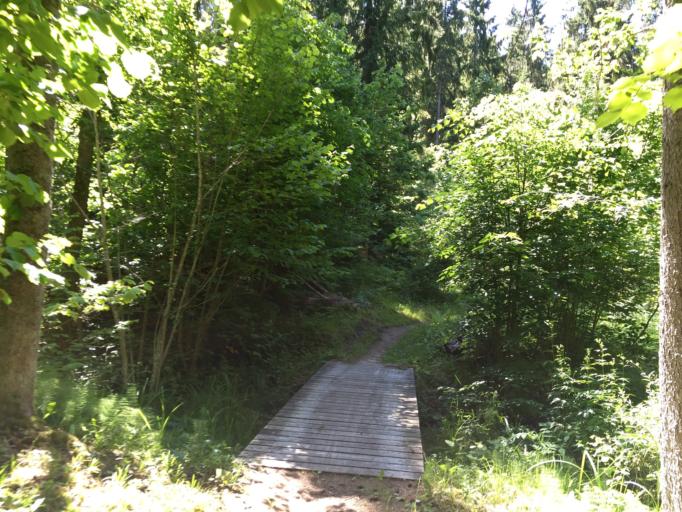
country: LV
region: Sigulda
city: Sigulda
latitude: 57.2214
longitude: 24.9081
